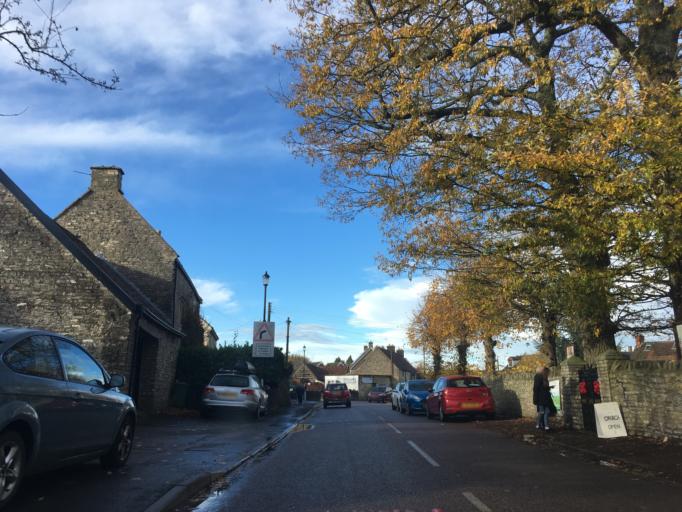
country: GB
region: England
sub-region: South Gloucestershire
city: Pucklechurch
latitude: 51.4866
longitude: -2.4349
